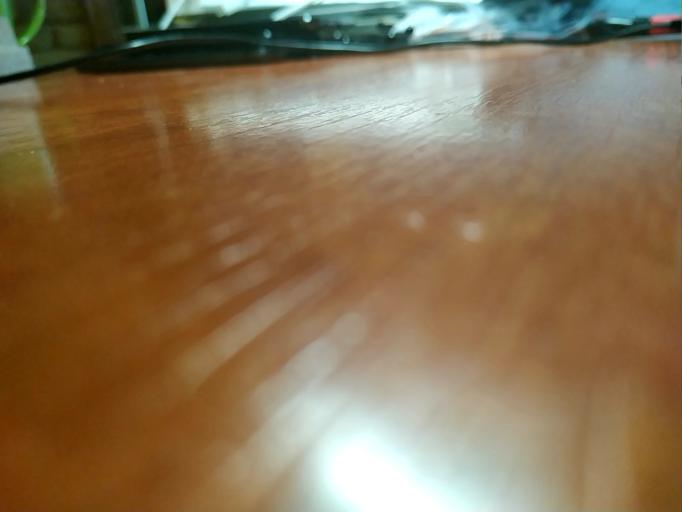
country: RU
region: Tverskaya
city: Toropets
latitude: 56.5112
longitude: 31.2101
